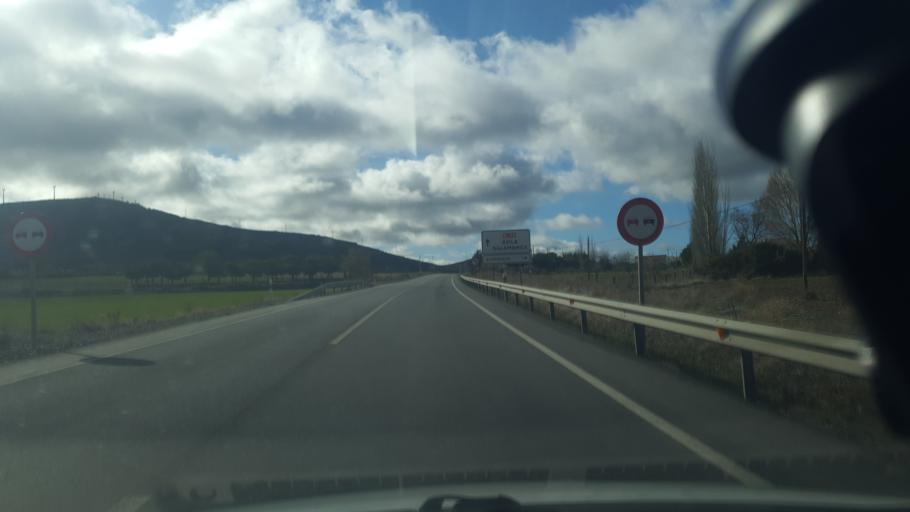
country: ES
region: Castille and Leon
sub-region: Provincia de Avila
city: Ojos-Albos
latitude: 40.7439
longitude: -4.4660
